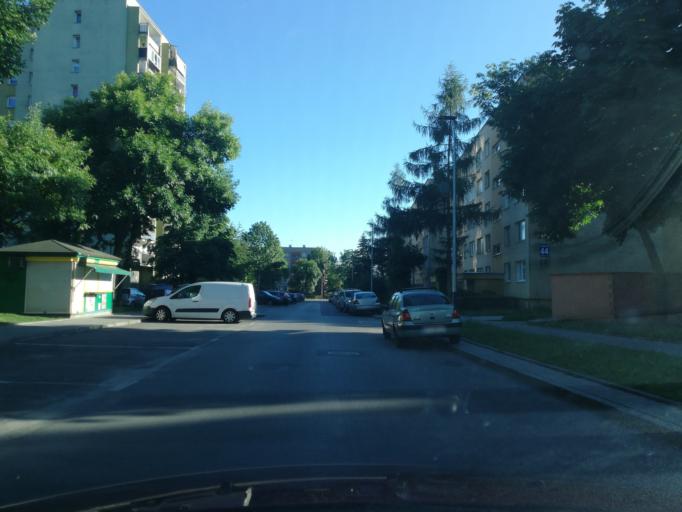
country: PL
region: Lesser Poland Voivodeship
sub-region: Krakow
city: Krakow
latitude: 50.0845
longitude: 20.0098
